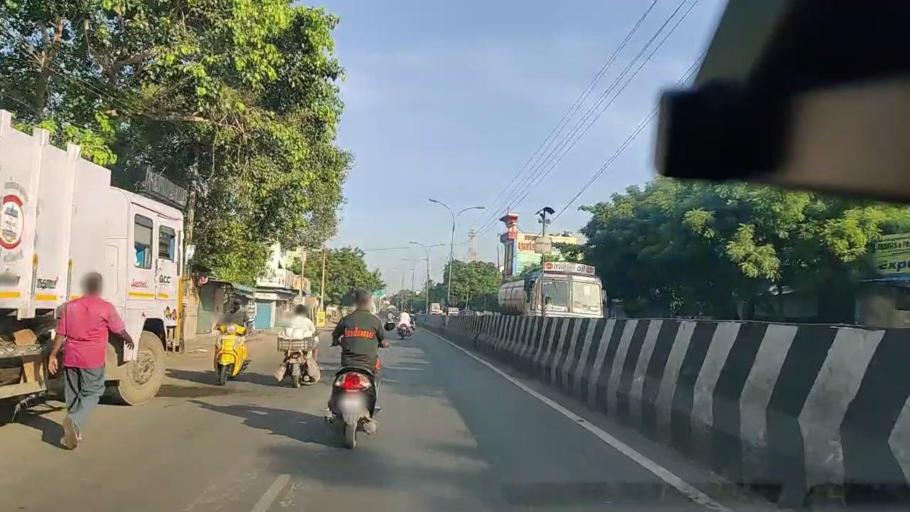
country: IN
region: Tamil Nadu
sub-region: Thiruvallur
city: Chinnasekkadu
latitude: 13.1254
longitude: 80.2463
